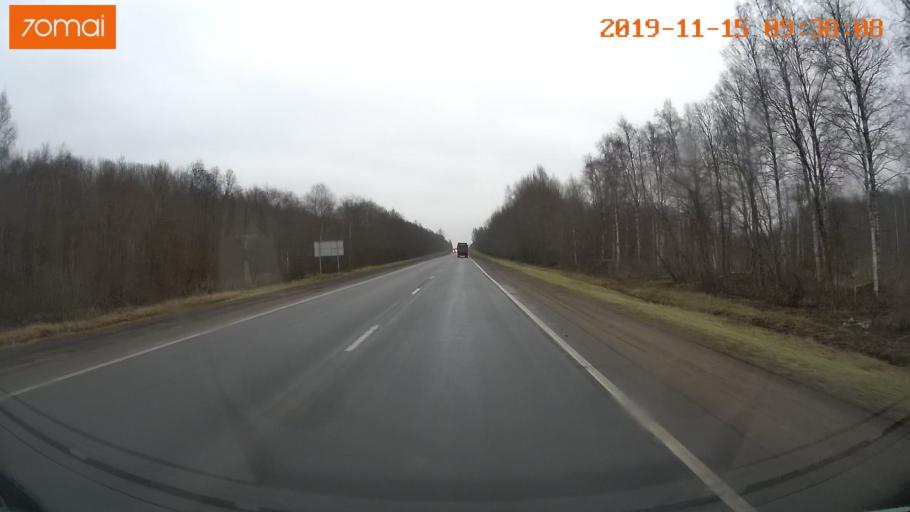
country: RU
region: Vologda
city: Sheksna
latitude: 59.2347
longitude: 38.4497
